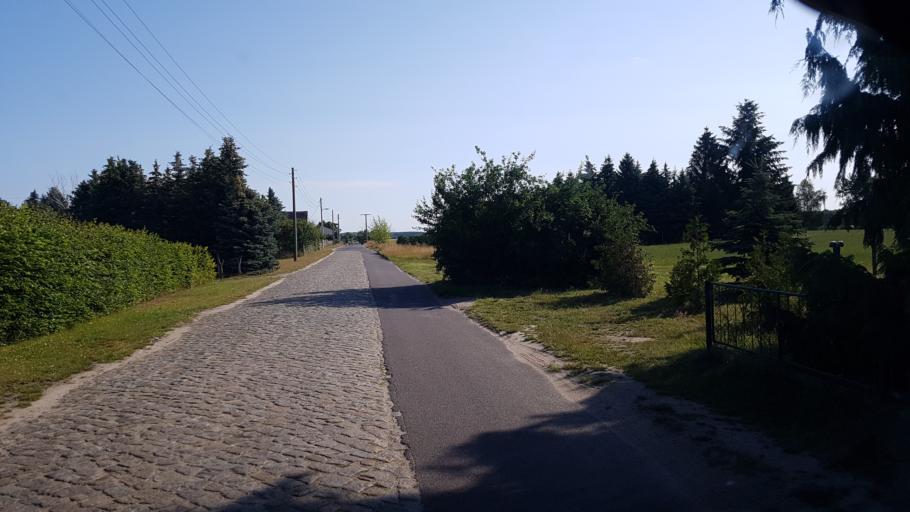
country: DE
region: Brandenburg
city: Sallgast
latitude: 51.5916
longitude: 13.8530
